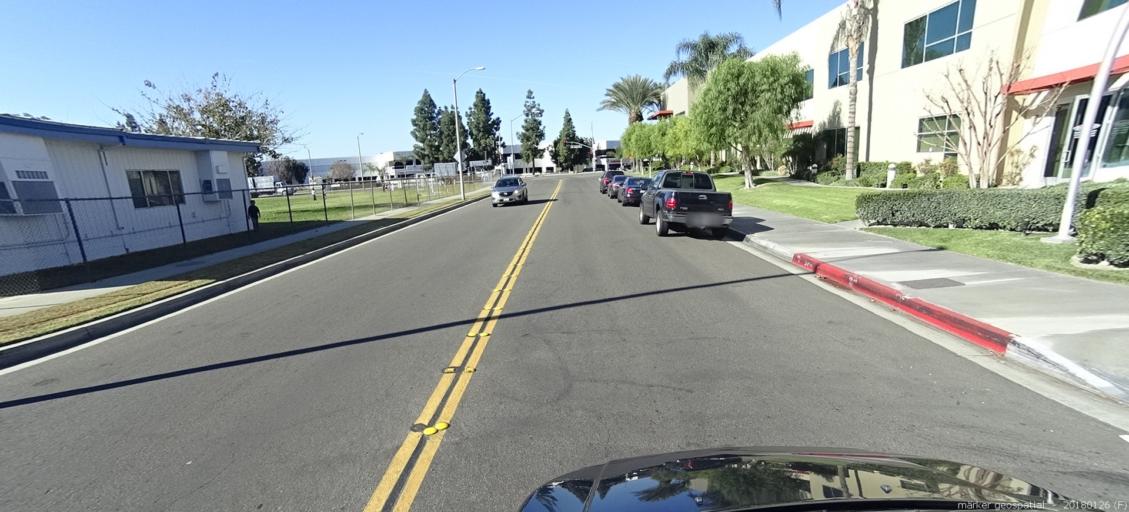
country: US
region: California
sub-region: Los Angeles County
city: Walnut
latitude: 34.0029
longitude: -117.8542
